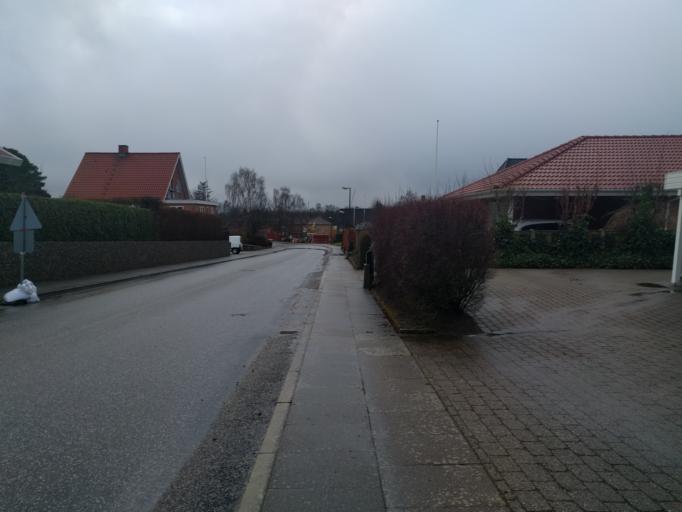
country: DK
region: Central Jutland
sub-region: Viborg Kommune
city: Viborg
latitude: 56.4514
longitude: 9.4411
